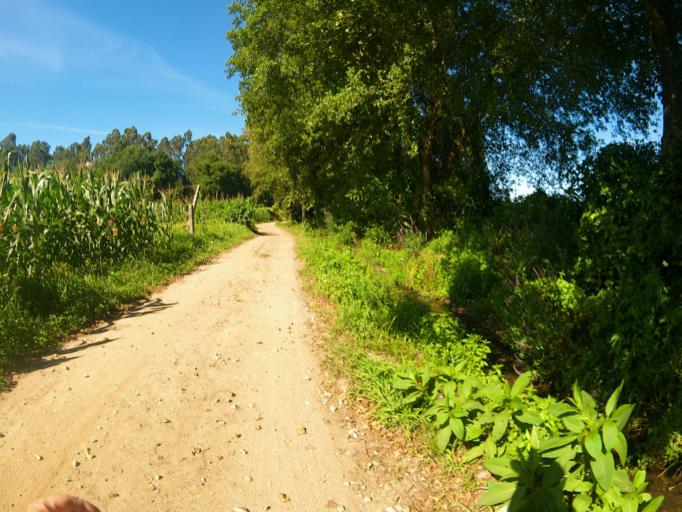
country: PT
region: Viana do Castelo
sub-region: Ponte de Lima
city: Ponte de Lima
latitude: 41.7276
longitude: -8.6673
